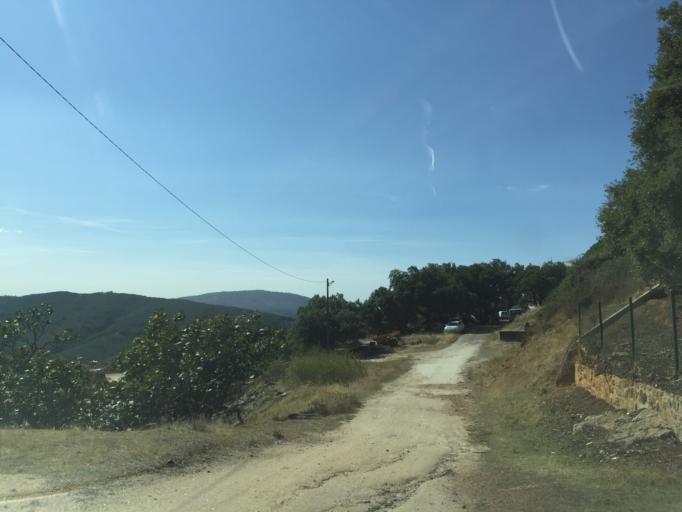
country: PT
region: Portalegre
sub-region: Marvao
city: Marvao
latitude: 39.3940
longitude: -7.3721
